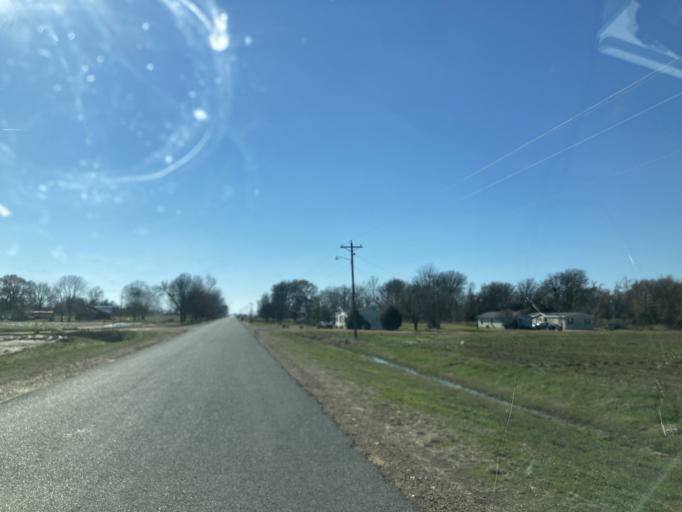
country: US
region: Mississippi
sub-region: Yazoo County
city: Yazoo City
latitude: 32.9710
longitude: -90.5952
